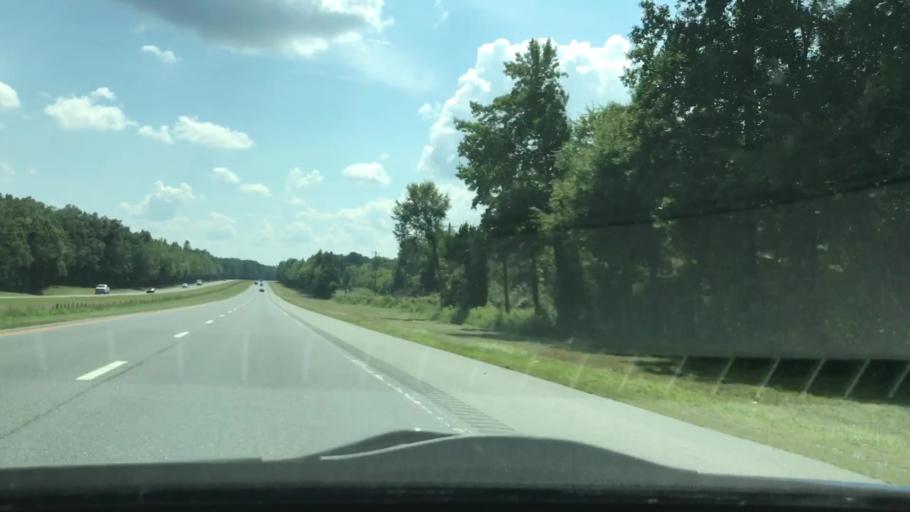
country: US
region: North Carolina
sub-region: Randolph County
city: Randleman
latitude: 35.8658
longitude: -79.8185
